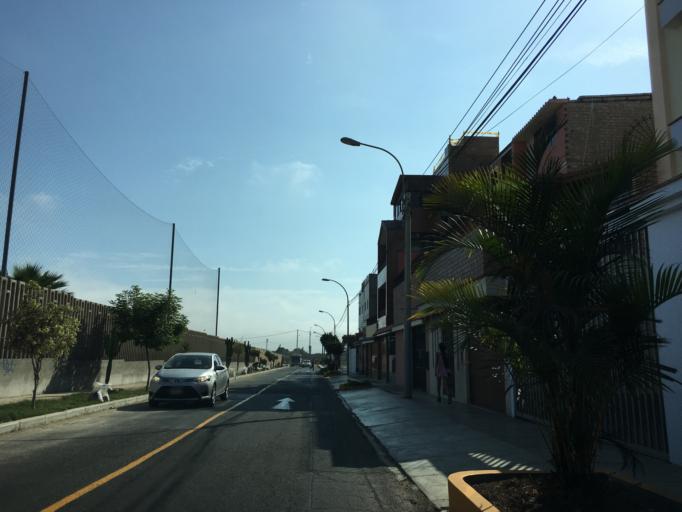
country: PE
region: Callao
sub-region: Callao
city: Callao
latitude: -12.0647
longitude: -77.0802
